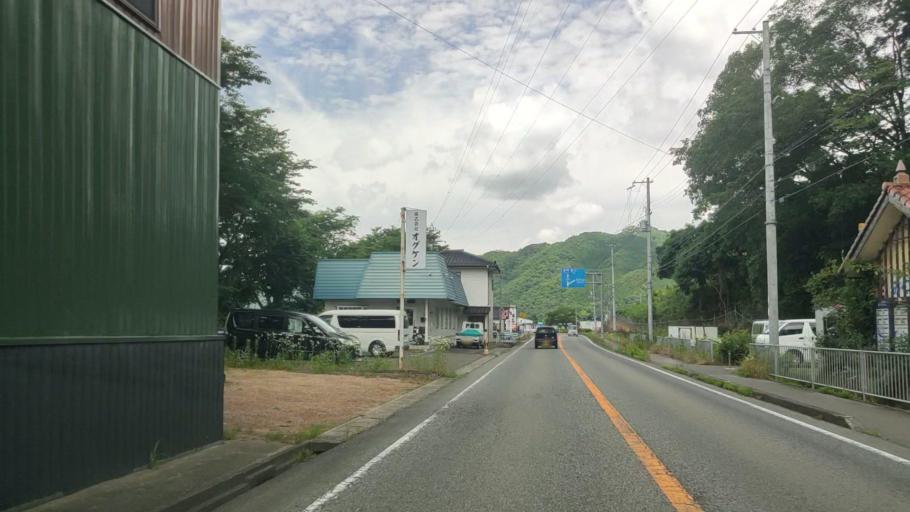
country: JP
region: Hyogo
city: Toyooka
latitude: 35.3511
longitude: 134.8413
